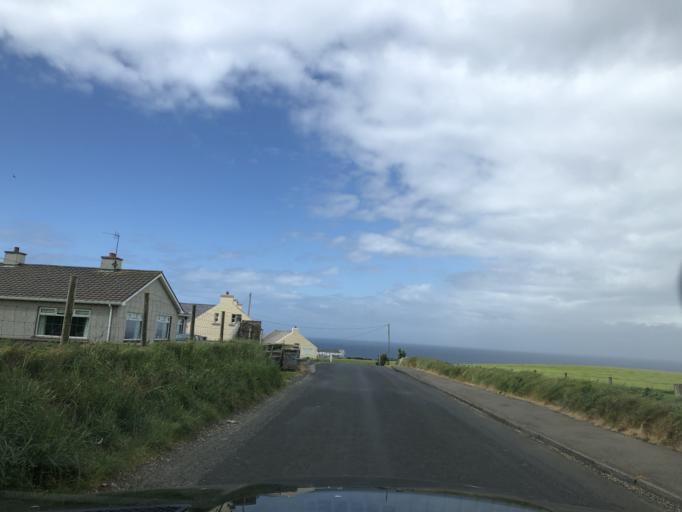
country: GB
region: Northern Ireland
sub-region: Moyle District
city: Ballycastle
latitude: 55.2376
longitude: -6.3655
